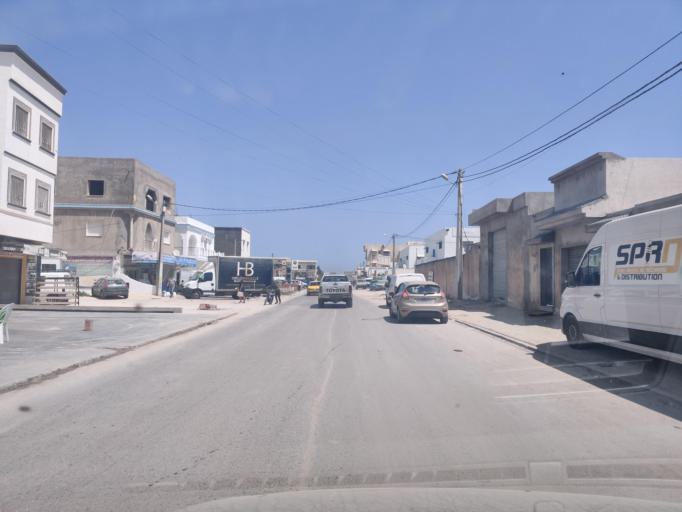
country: TN
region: Tunis
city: Al Marsa
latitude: 36.8732
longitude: 10.3025
